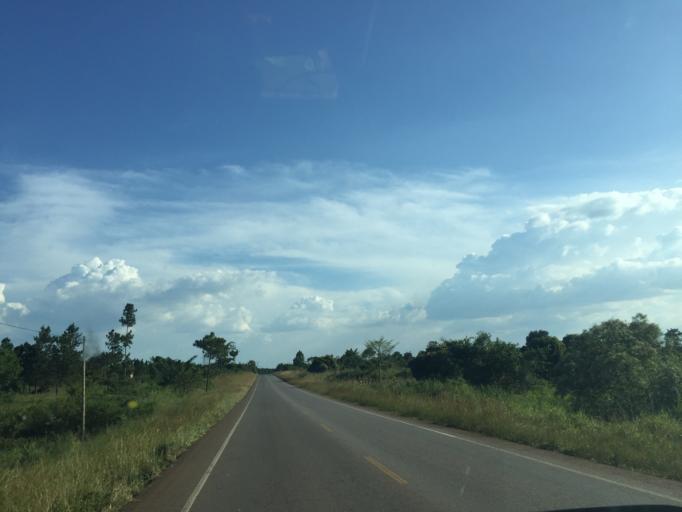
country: UG
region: Central Region
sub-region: Nakasongola District
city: Nakasongola
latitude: 1.2297
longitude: 32.4643
